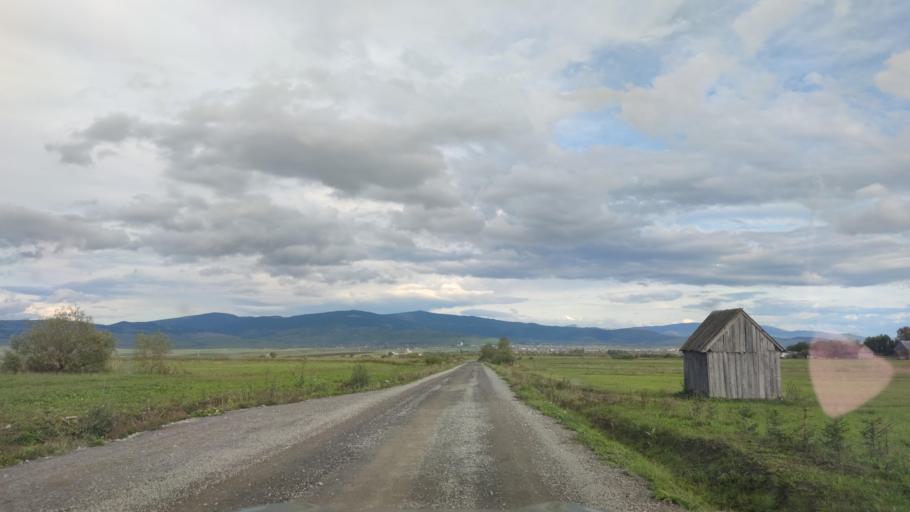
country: RO
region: Harghita
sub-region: Comuna Remetea
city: Remetea
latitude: 46.8165
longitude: 25.4170
